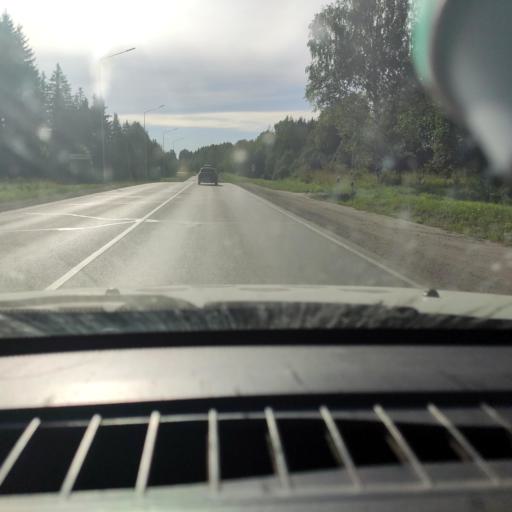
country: RU
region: Kirov
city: Vakhrushi
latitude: 58.6779
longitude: 49.9990
